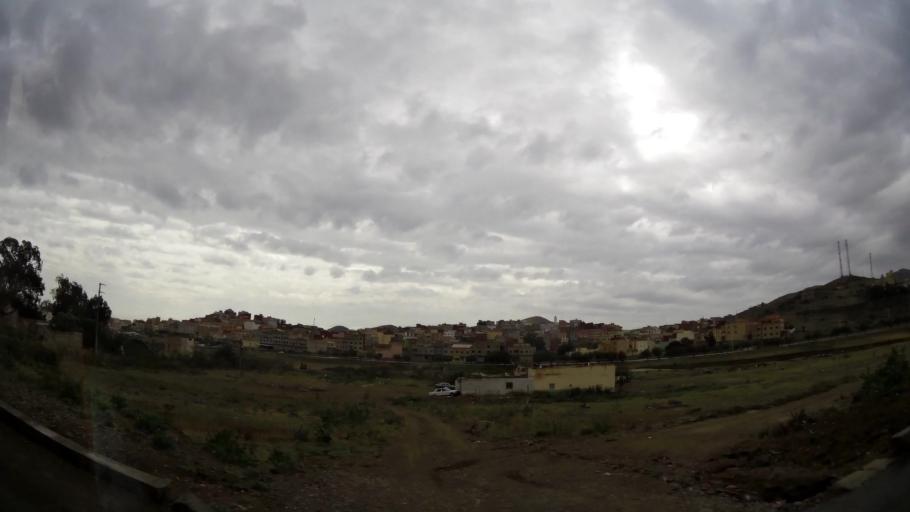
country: MA
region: Oriental
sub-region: Nador
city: Nador
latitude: 35.1485
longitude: -3.0083
